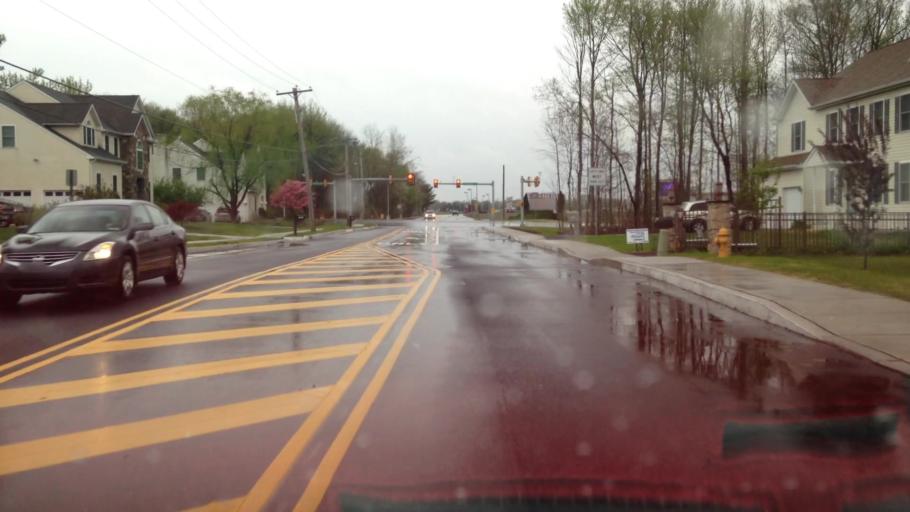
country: US
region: Pennsylvania
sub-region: Bucks County
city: Eddington
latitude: 40.1133
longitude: -74.9491
